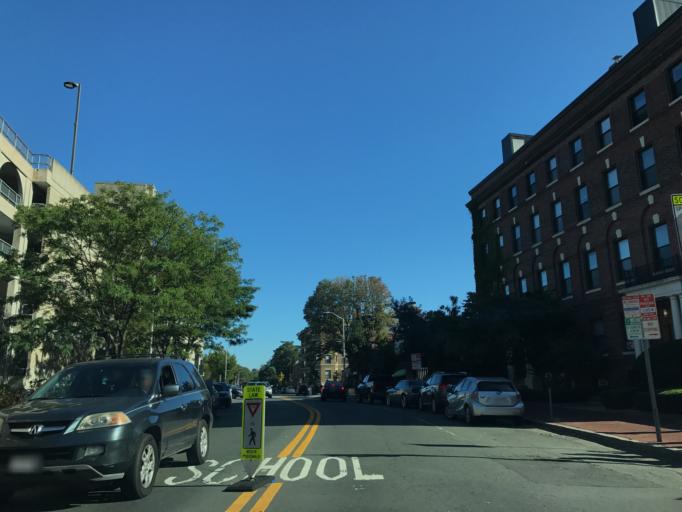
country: US
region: Massachusetts
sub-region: Middlesex County
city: Cambridge
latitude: 42.3744
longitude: -71.1136
